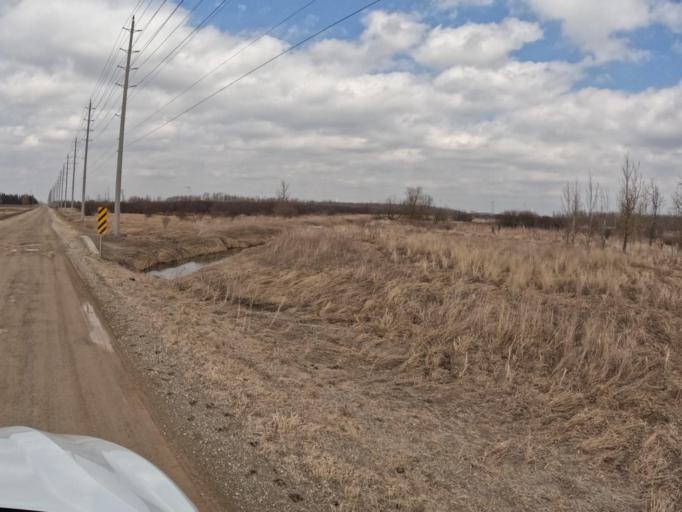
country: CA
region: Ontario
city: Shelburne
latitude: 44.0228
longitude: -80.3134
